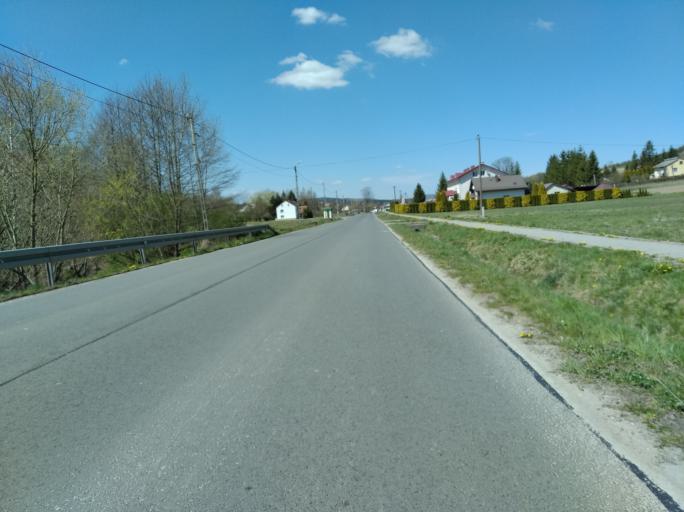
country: PL
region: Subcarpathian Voivodeship
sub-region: Powiat brzozowski
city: Dydnia
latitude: 49.6862
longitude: 22.1716
